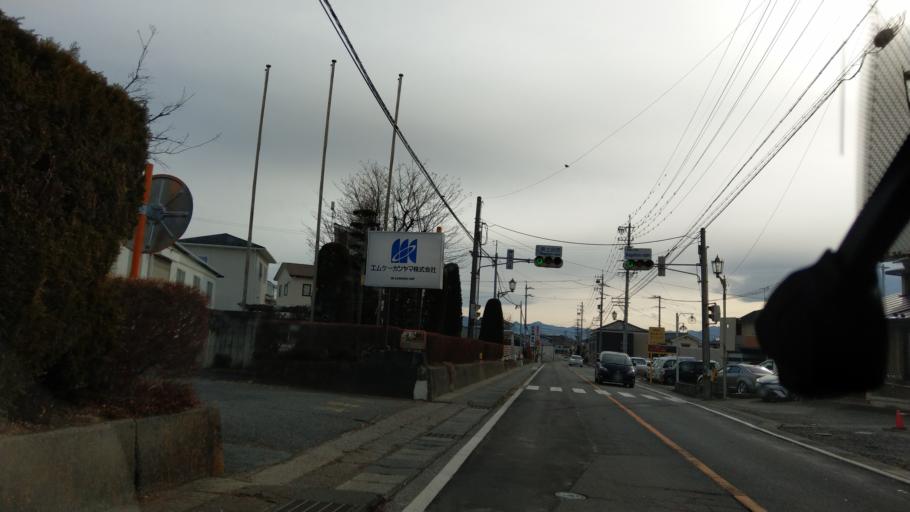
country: JP
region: Nagano
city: Komoro
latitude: 36.2853
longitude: 138.4631
